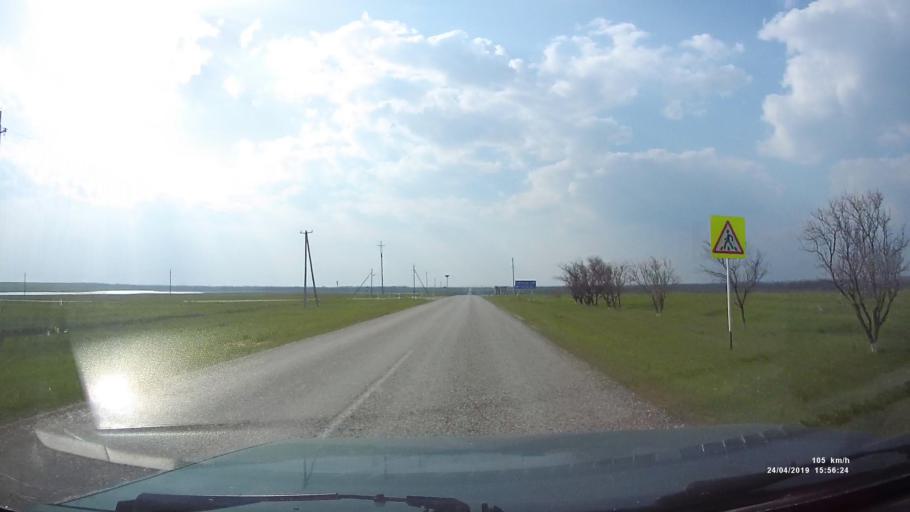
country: RU
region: Kalmykiya
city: Yashalta
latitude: 46.5974
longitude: 42.5296
